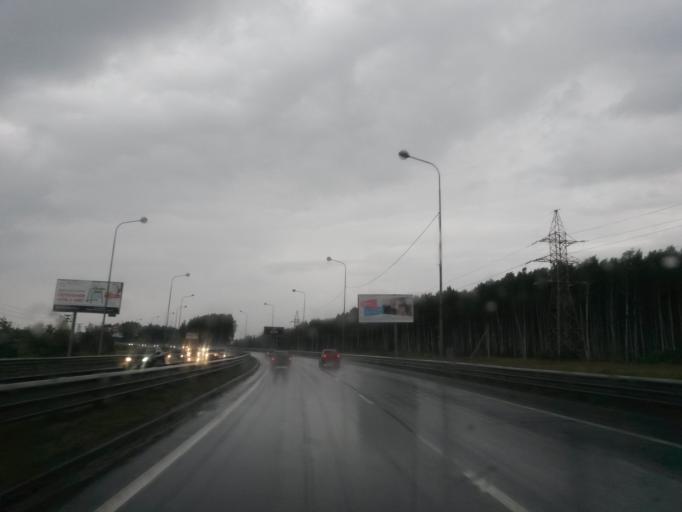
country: RU
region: Jaroslavl
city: Yaroslavl
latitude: 57.6836
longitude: 39.8847
